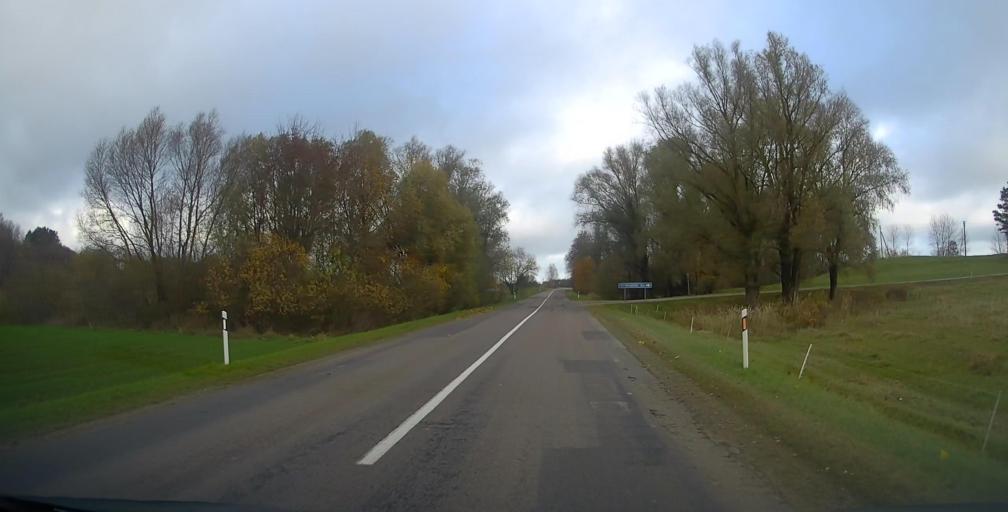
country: LT
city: Kybartai
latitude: 54.5013
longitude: 22.7131
